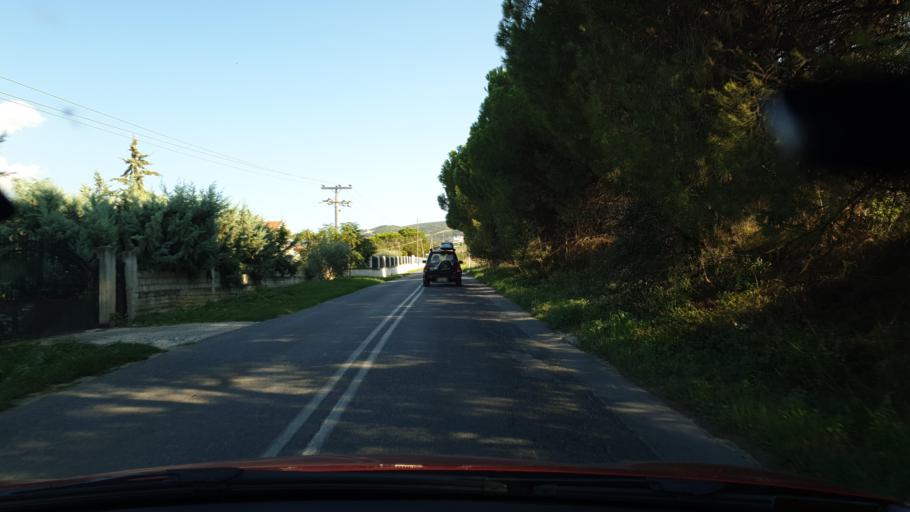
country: GR
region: Central Macedonia
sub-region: Nomos Thessalonikis
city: Agia Paraskevi
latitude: 40.4880
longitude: 23.0398
